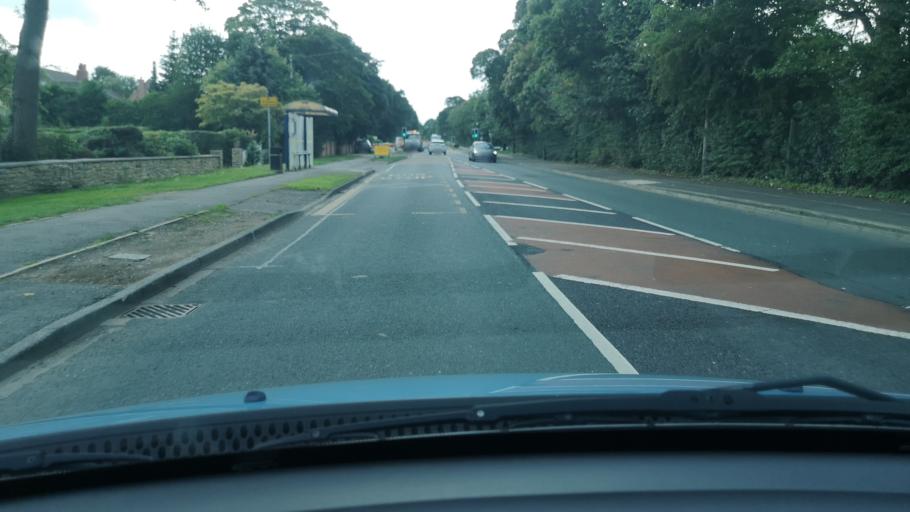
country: GB
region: England
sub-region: Doncaster
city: Kirk Sandall
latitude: 53.5511
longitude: -1.0718
